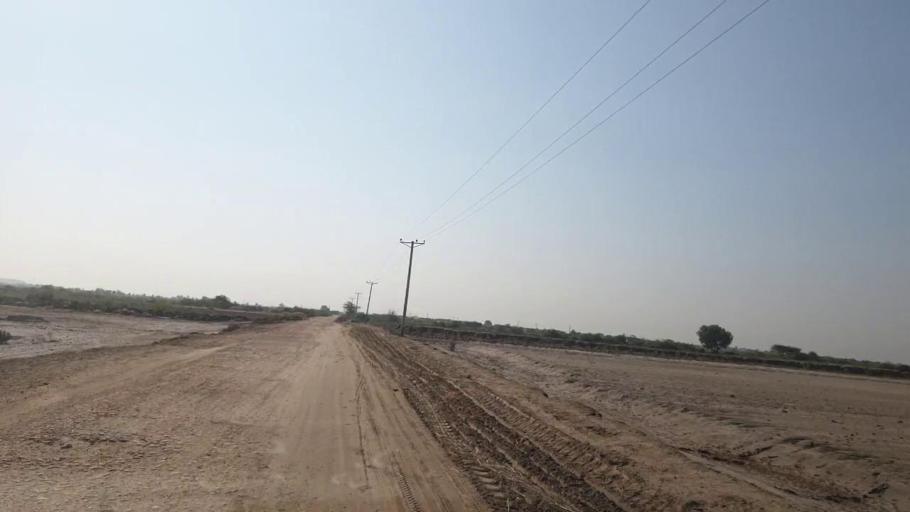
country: PK
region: Sindh
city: Thatta
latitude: 24.7362
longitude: 67.7942
